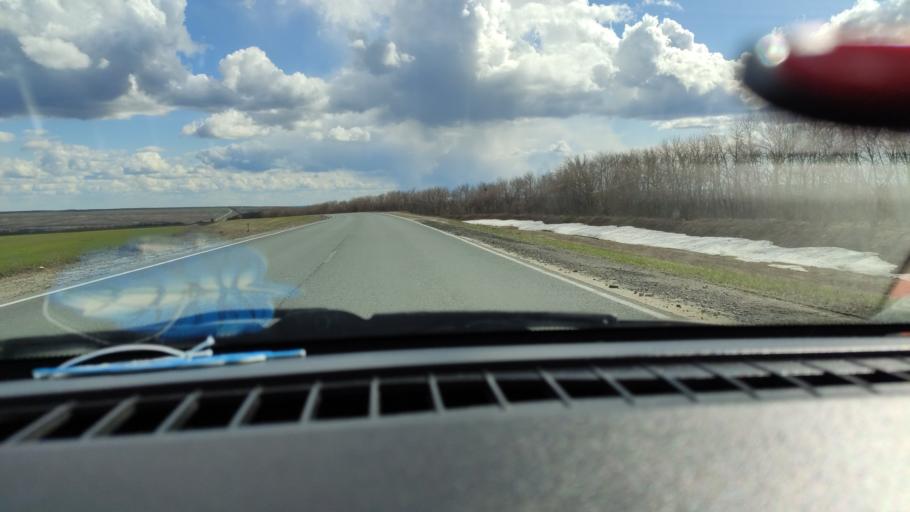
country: RU
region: Saratov
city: Dukhovnitskoye
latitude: 52.7637
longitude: 48.2395
